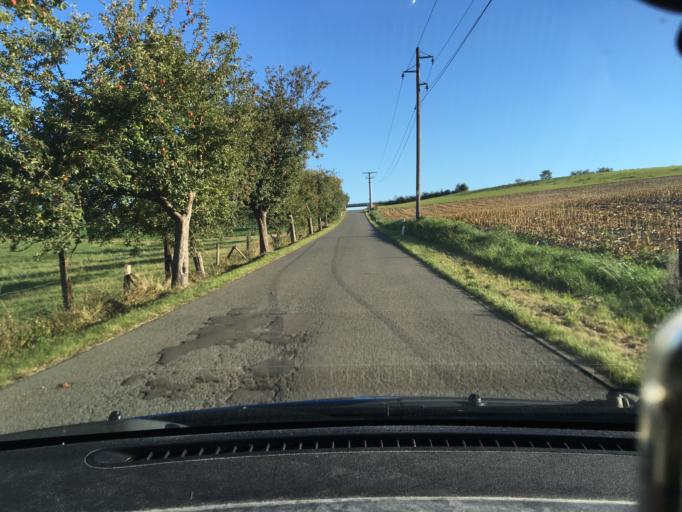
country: DE
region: Lower Saxony
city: Messenkamp
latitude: 52.2253
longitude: 9.4120
